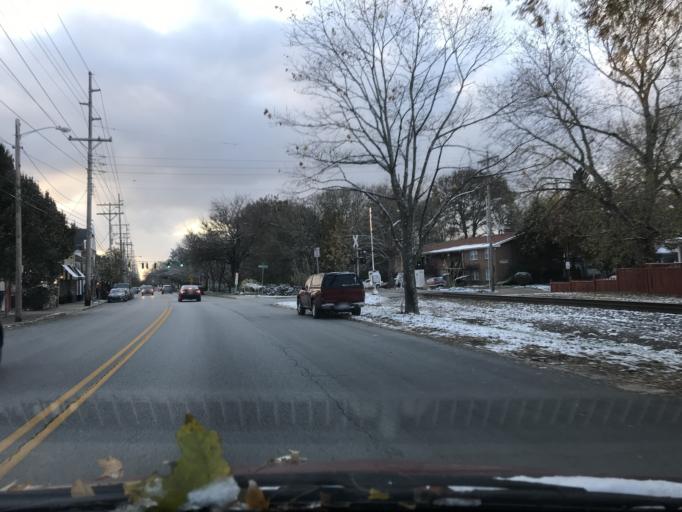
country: US
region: Kentucky
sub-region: Jefferson County
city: Indian Hills
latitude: 38.2548
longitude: -85.6917
